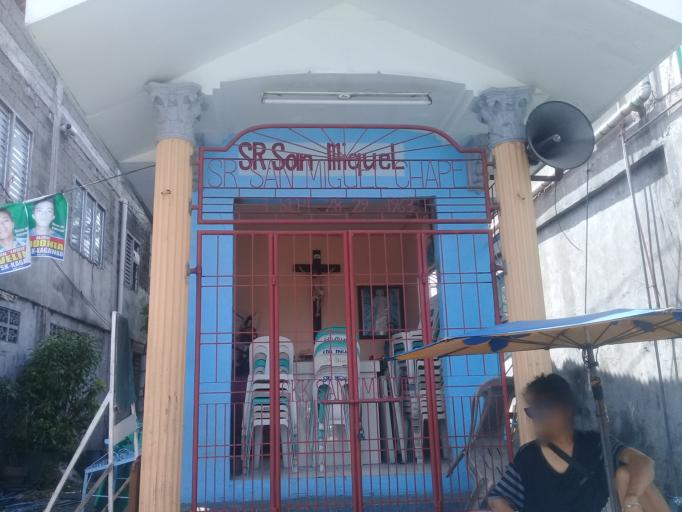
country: PH
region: Davao
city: Davao
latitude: 7.0689
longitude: 125.6214
